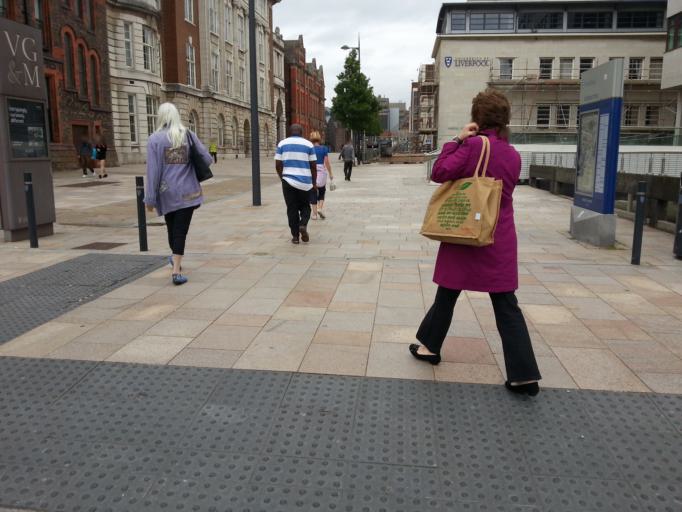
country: GB
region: England
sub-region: Liverpool
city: Liverpool
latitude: 53.4060
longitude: -2.9659
